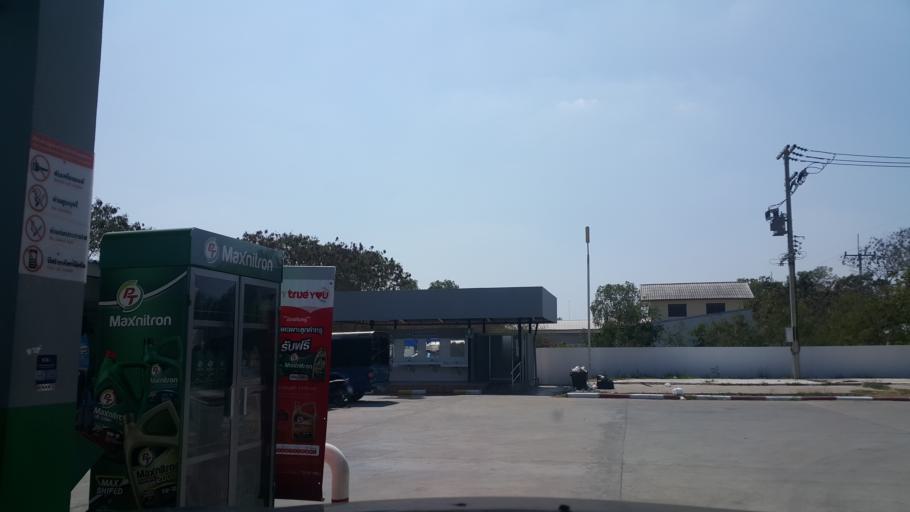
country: TH
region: Nakhon Ratchasima
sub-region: Amphoe Kaeng Sanam Nang
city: Kaeng Sanam Nang
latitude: 15.6881
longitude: 102.3313
